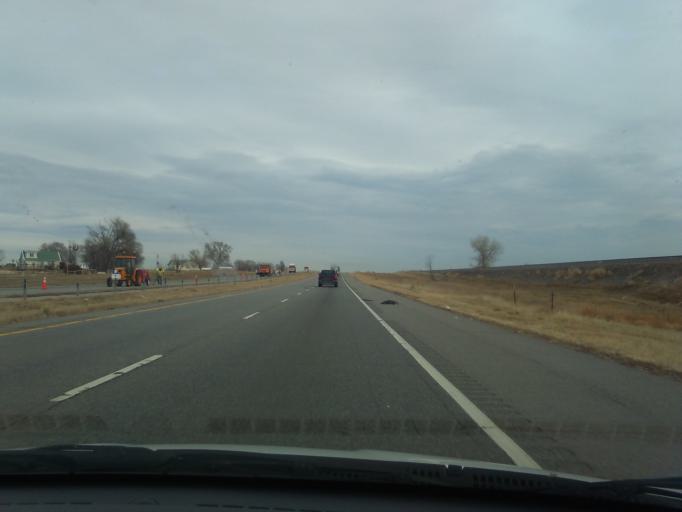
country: US
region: Colorado
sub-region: Weld County
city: Hudson
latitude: 40.0456
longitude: -104.6698
